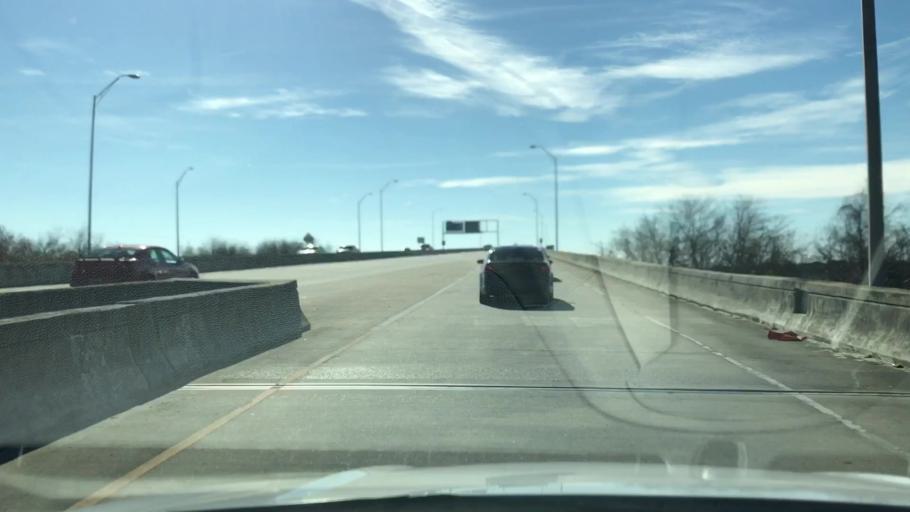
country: US
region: South Carolina
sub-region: Charleston County
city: Charleston
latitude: 32.7743
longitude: -79.9579
